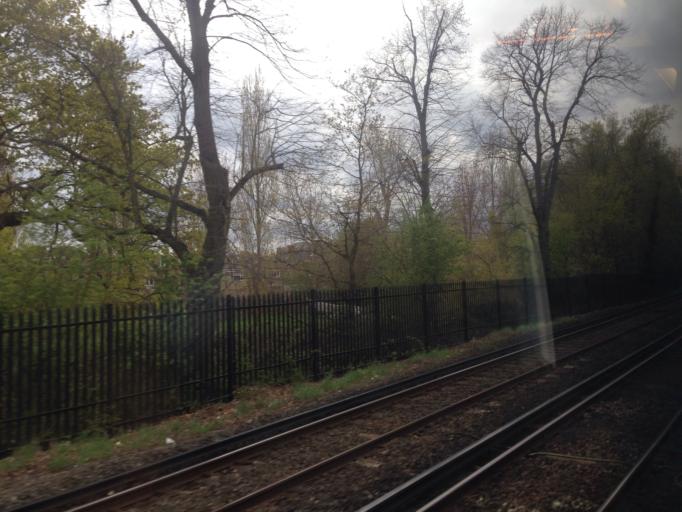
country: GB
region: England
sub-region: Greater London
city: Brixton Hill
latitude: 51.4372
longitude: -0.1410
